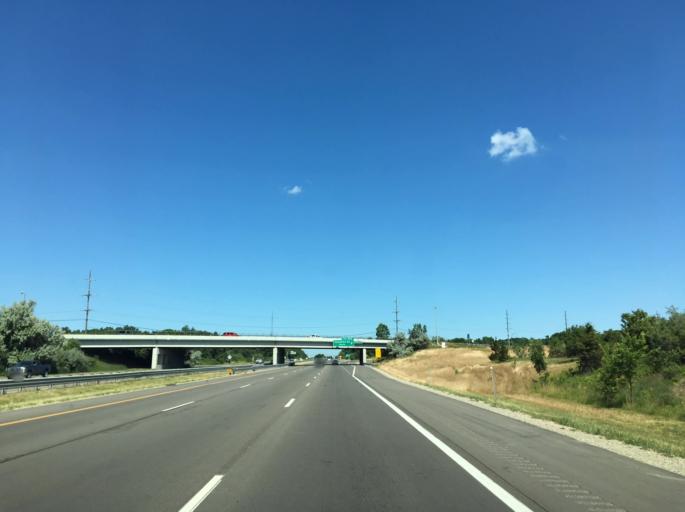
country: US
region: Michigan
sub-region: Oakland County
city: Clarkston
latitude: 42.7350
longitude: -83.3780
